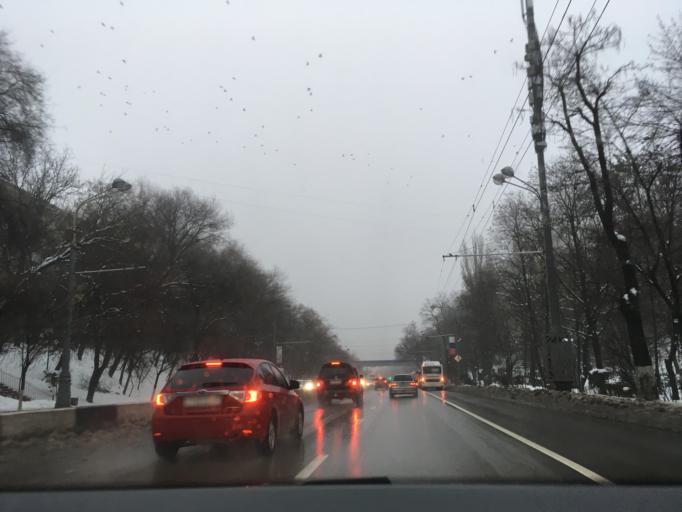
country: RU
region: Rostov
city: Rostov-na-Donu
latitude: 47.2113
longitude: 39.6831
